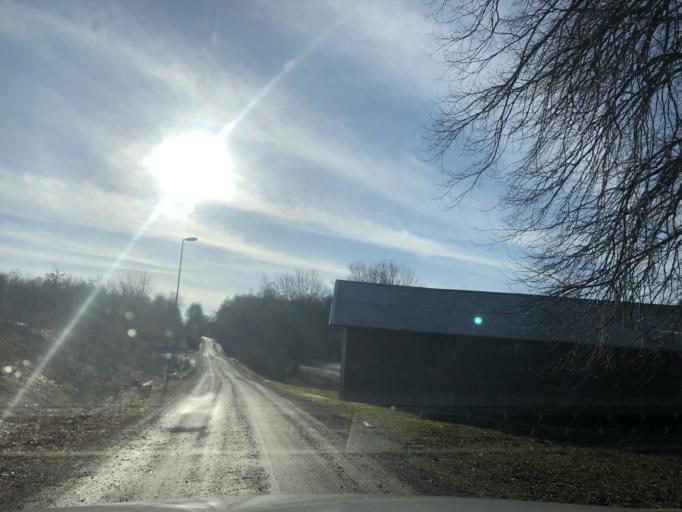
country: SE
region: Vaestra Goetaland
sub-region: Ulricehamns Kommun
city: Ulricehamn
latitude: 57.7995
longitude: 13.4428
